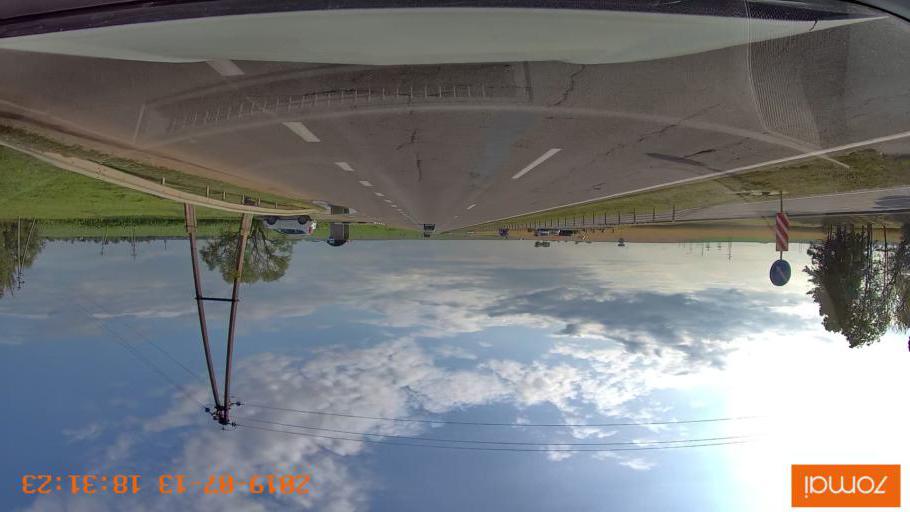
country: BY
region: Minsk
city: Dukora
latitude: 53.6697
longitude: 27.9356
